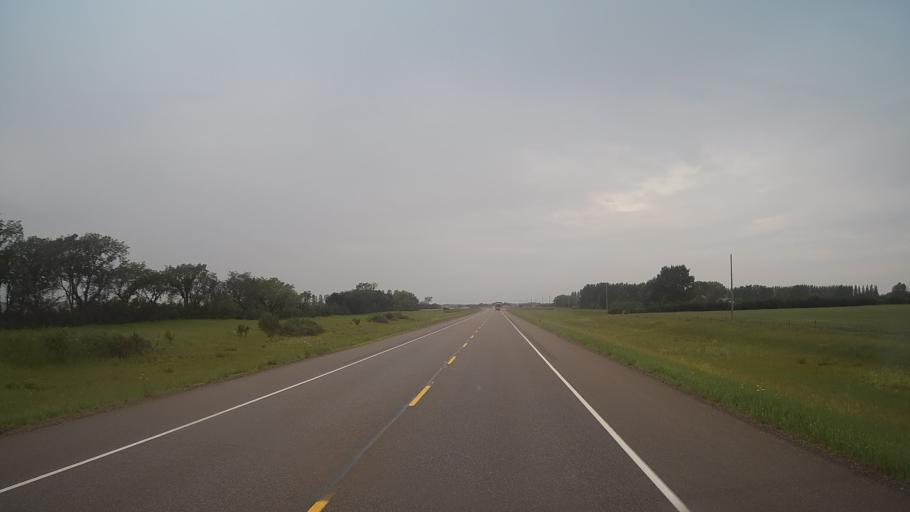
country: CA
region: Saskatchewan
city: Dalmeny
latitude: 52.1292
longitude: -106.8750
